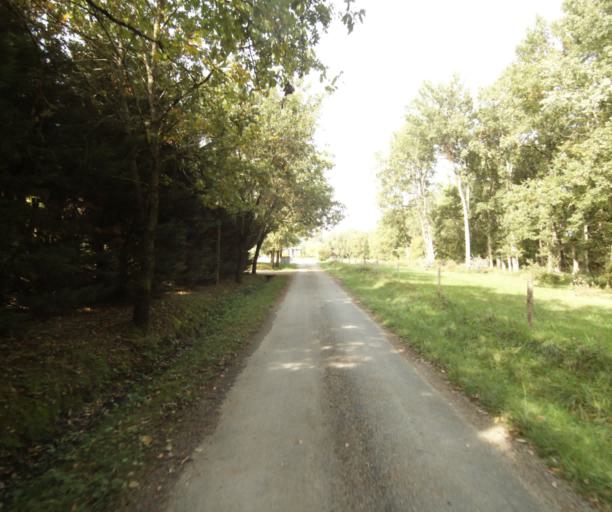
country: FR
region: Midi-Pyrenees
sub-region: Departement du Tarn-et-Garonne
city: Orgueil
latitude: 43.9092
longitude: 1.4124
